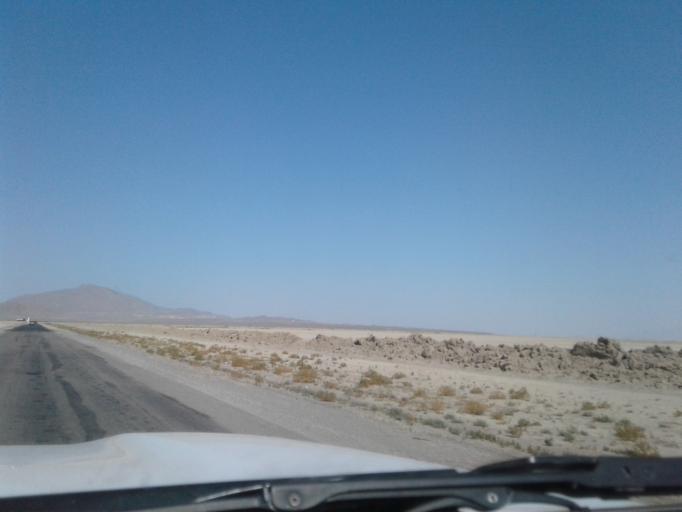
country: TM
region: Balkan
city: Gumdag
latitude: 39.2362
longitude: 54.6973
